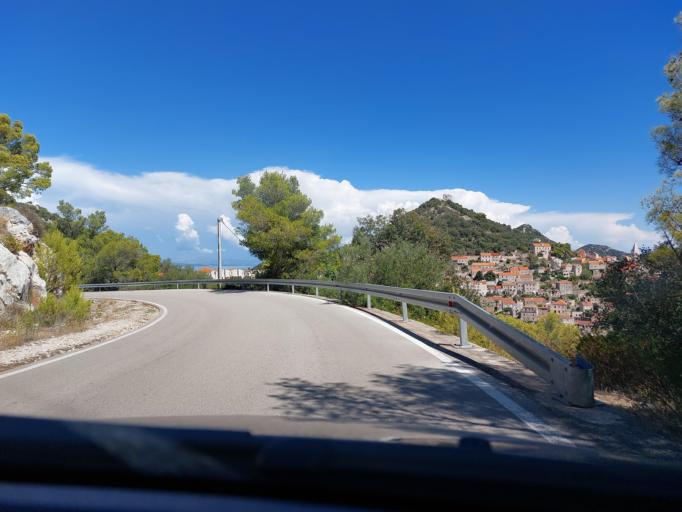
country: HR
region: Dubrovacko-Neretvanska
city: Smokvica
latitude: 42.7670
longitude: 16.8921
